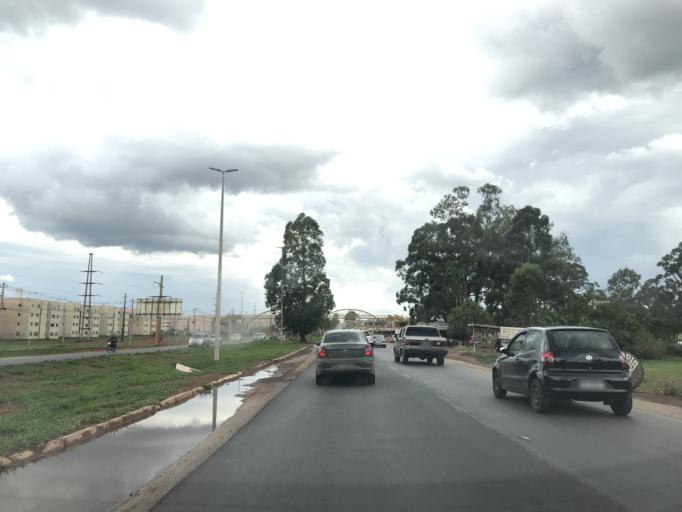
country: BR
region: Federal District
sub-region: Brasilia
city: Brasilia
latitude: -15.8905
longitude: -48.0578
